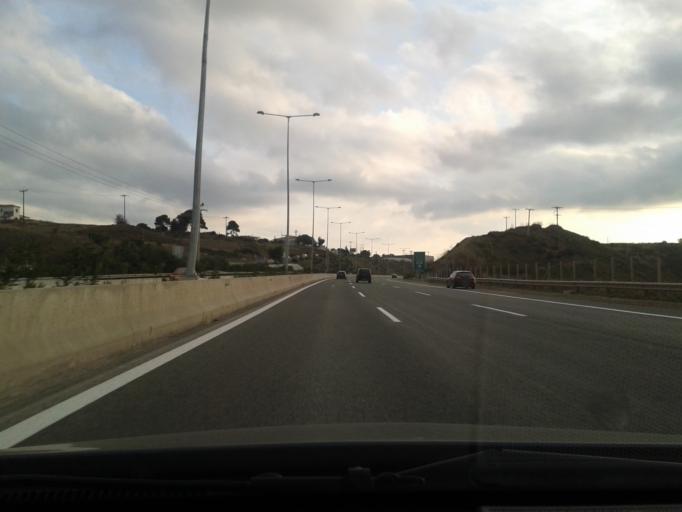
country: GR
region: Attica
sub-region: Nomarchia Anatolikis Attikis
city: Agios Stefanos
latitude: 38.1566
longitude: 23.8554
